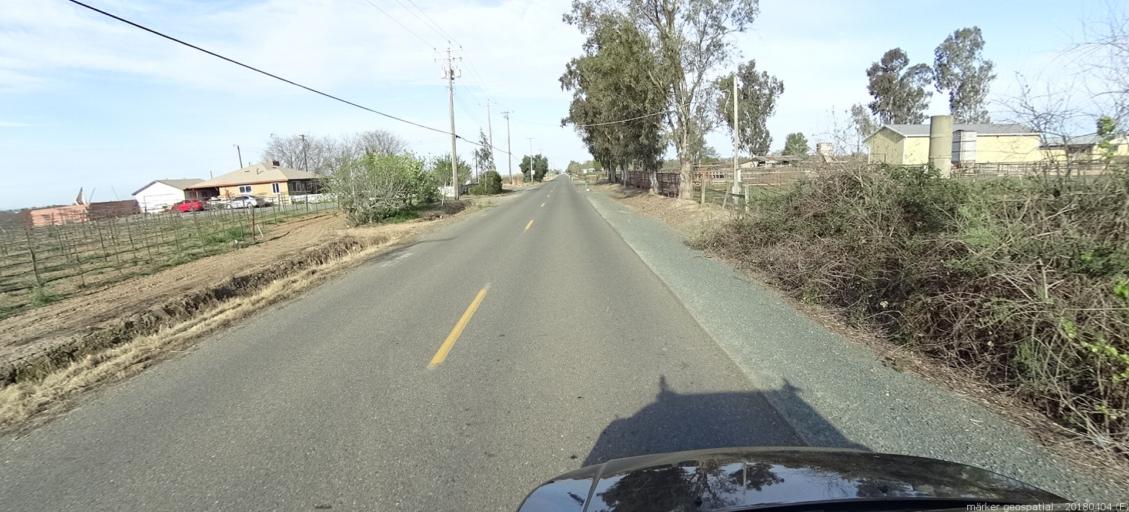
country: US
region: California
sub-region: Sacramento County
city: Herald
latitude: 38.3257
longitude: -121.2776
